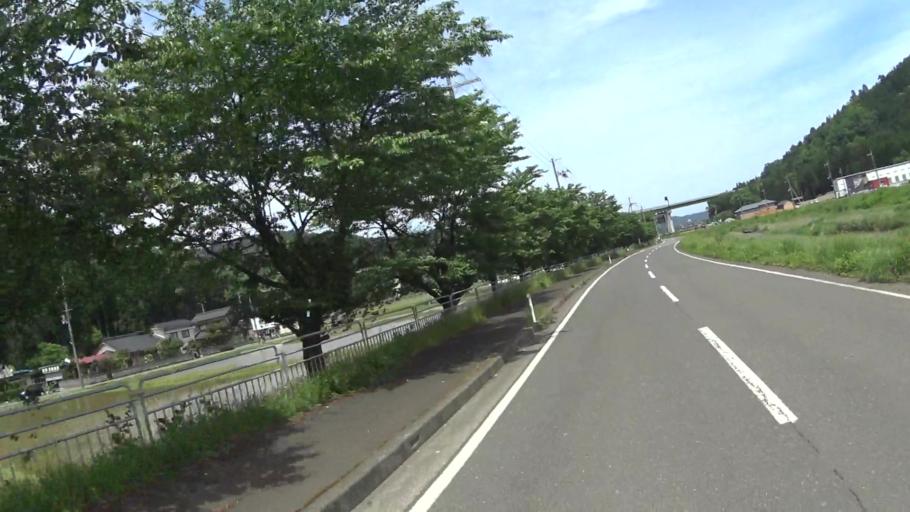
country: JP
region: Fukui
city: Obama
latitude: 35.4458
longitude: 135.5515
